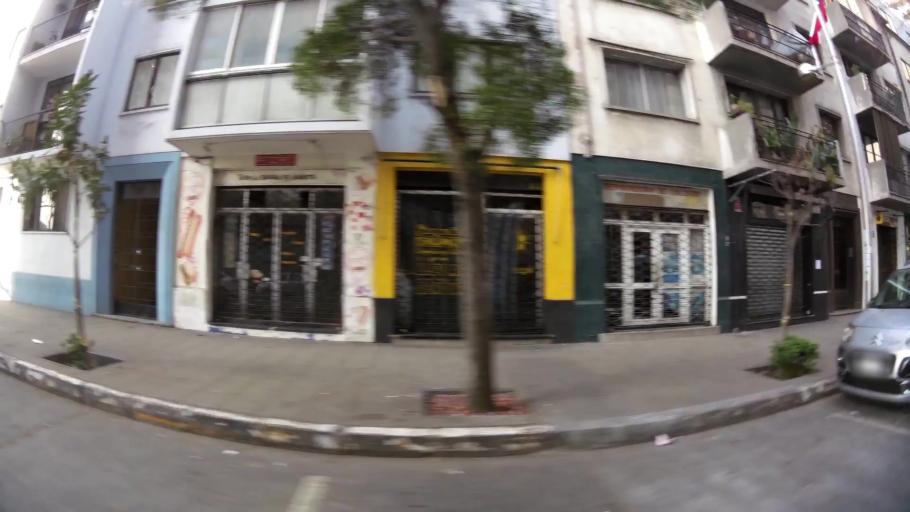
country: CL
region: Santiago Metropolitan
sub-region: Provincia de Santiago
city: Santiago
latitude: -33.4423
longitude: -70.6590
